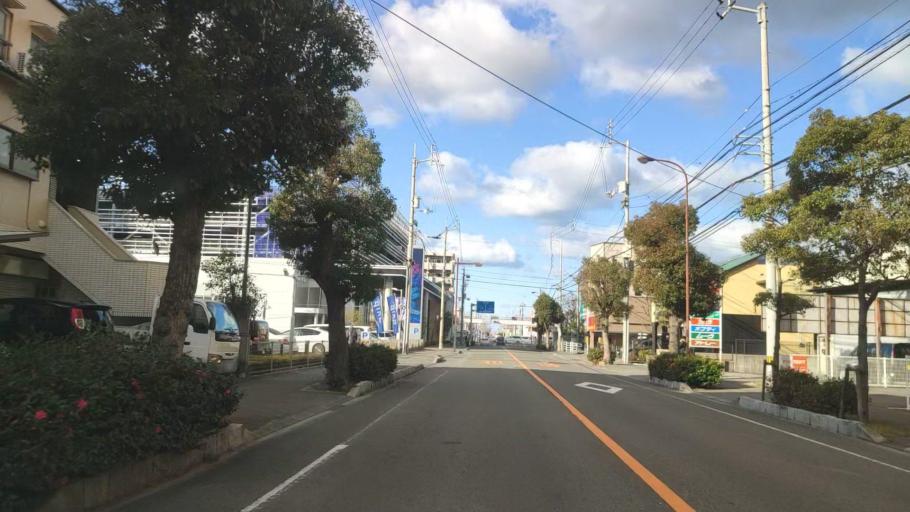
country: JP
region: Ehime
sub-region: Shikoku-chuo Shi
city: Matsuyama
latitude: 33.8286
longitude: 132.7462
